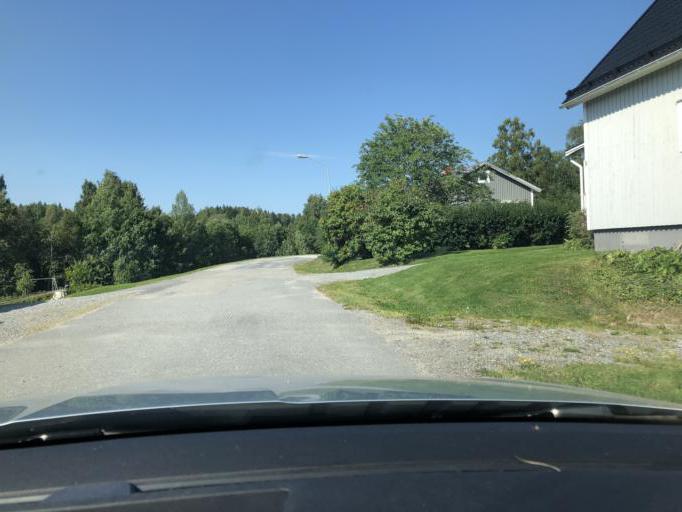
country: SE
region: Vaesternorrland
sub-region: OErnskoeldsviks Kommun
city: Bredbyn
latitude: 63.4475
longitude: 18.1068
